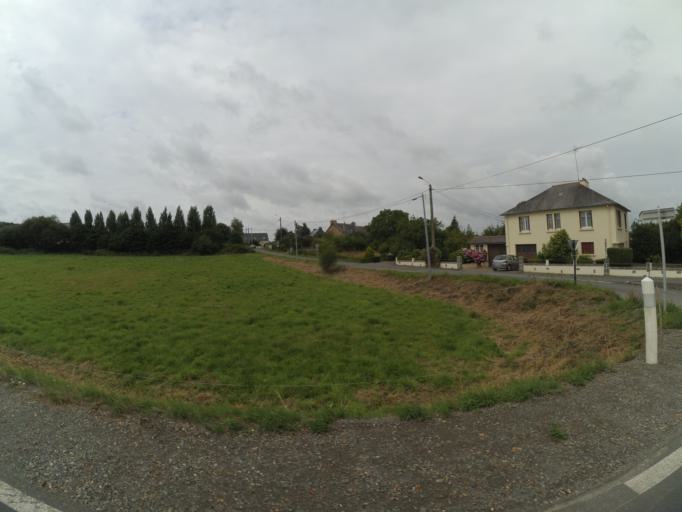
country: FR
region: Brittany
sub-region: Departement des Cotes-d'Armor
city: La Meaugon
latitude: 48.5189
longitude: -2.8147
